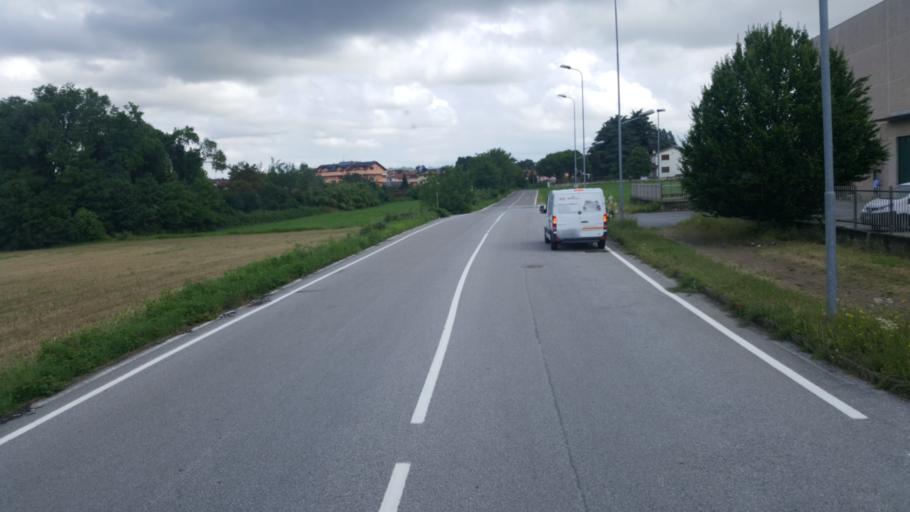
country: IT
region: Lombardy
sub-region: Provincia di Varese
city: Gerenzano
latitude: 45.6310
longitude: 9.0066
